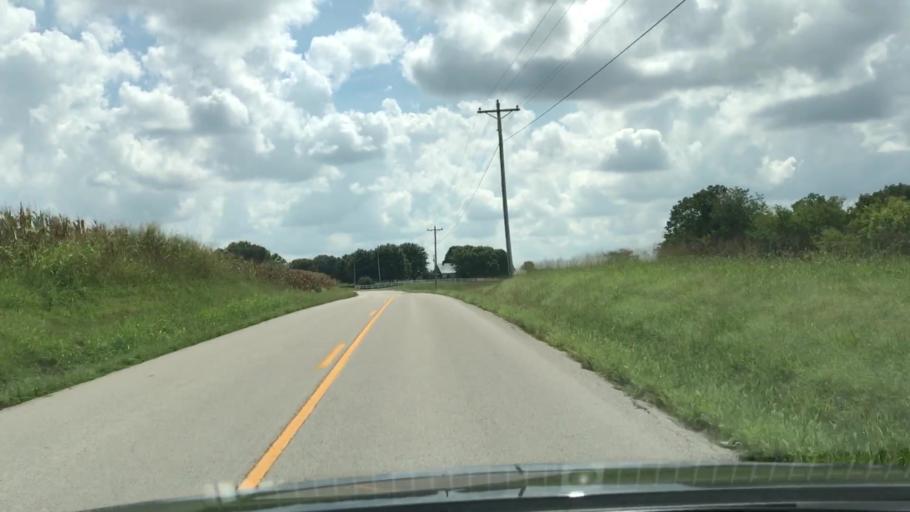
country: US
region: Kentucky
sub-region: Todd County
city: Elkton
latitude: 36.7898
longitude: -87.1363
